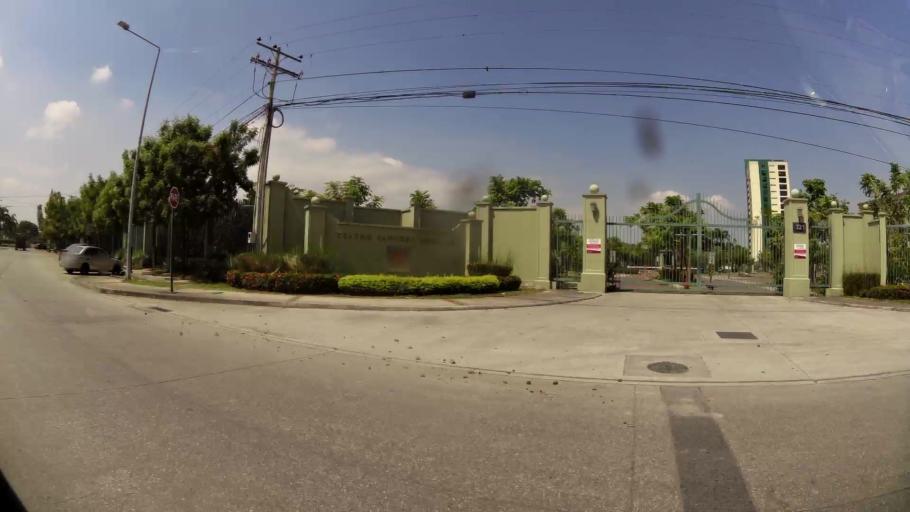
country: EC
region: Guayas
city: Eloy Alfaro
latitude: -2.1409
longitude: -79.8666
